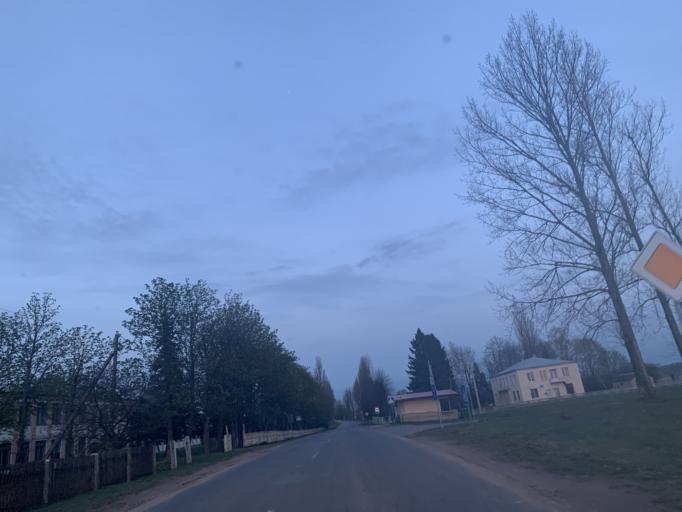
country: BY
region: Minsk
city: Snow
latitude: 53.1689
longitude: 26.5120
